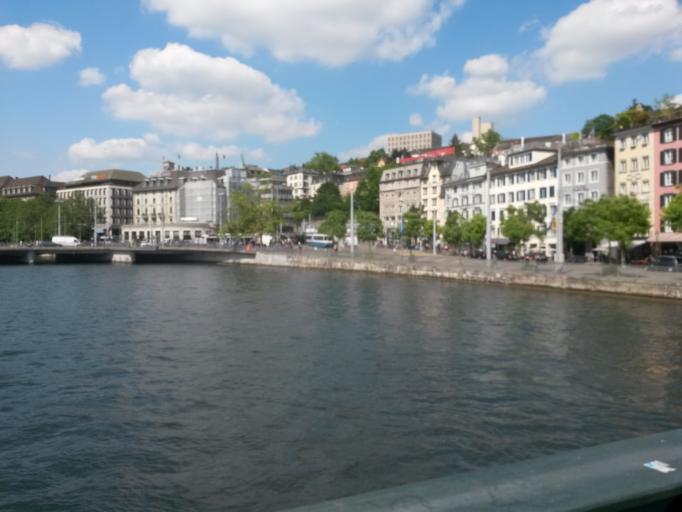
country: CH
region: Zurich
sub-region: Bezirk Zuerich
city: Zuerich (Kreis 1) / Lindenhof
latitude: 47.3756
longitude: 8.5428
